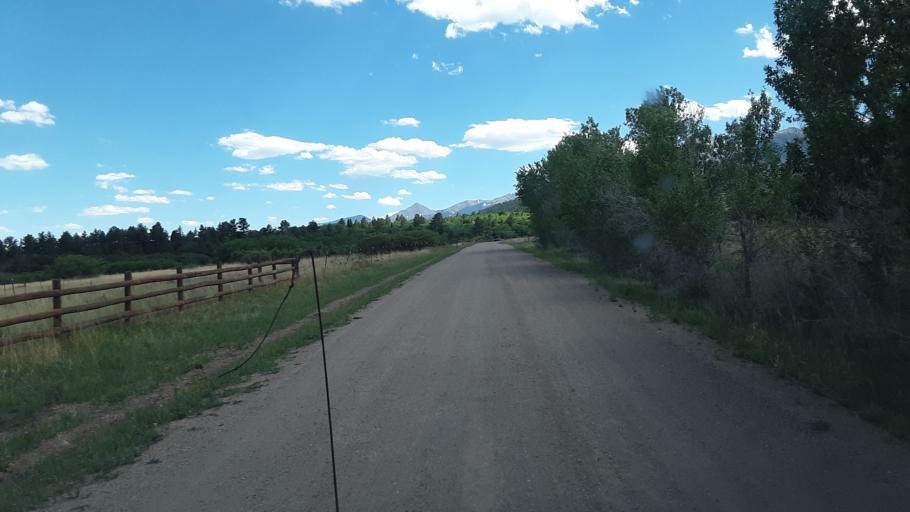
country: US
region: Colorado
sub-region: Custer County
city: Westcliffe
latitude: 38.2272
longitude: -105.5991
